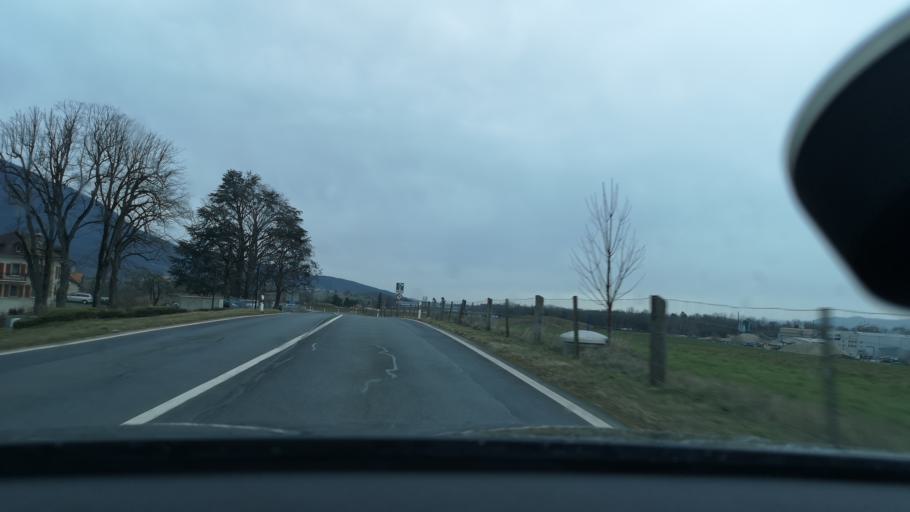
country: CH
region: Vaud
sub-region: Jura-Nord vaudois District
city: Grandson
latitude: 46.8235
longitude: 6.6679
